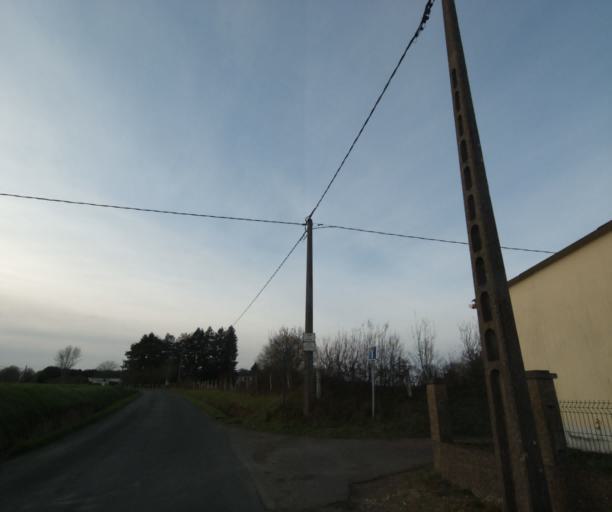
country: FR
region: Pays de la Loire
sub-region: Departement de la Sarthe
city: Rouillon
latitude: 48.0043
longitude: 0.1629
